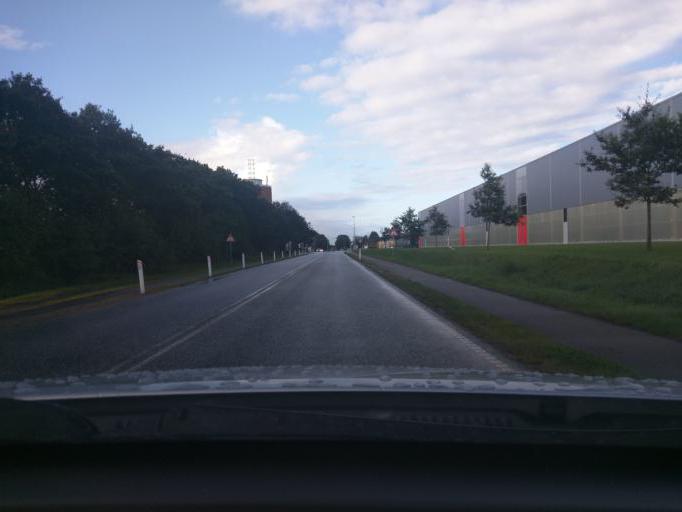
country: DK
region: Central Jutland
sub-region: Viborg Kommune
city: Viborg
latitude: 56.4646
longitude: 9.4076
